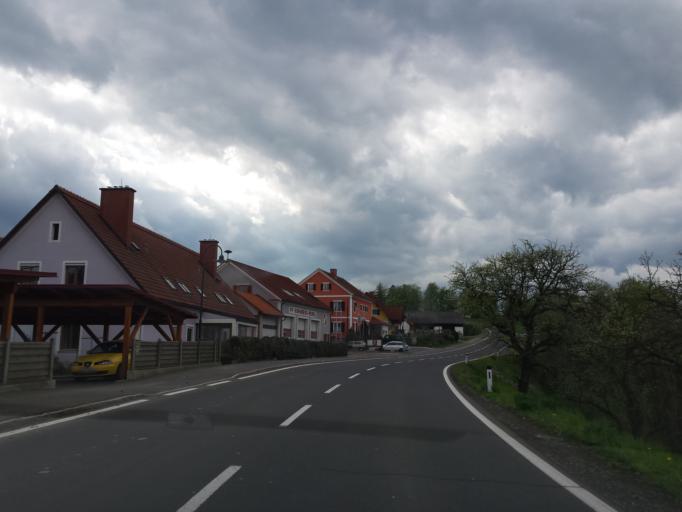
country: AT
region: Styria
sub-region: Politischer Bezirk Suedoststeiermark
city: Riegersburg
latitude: 46.9918
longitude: 15.9236
